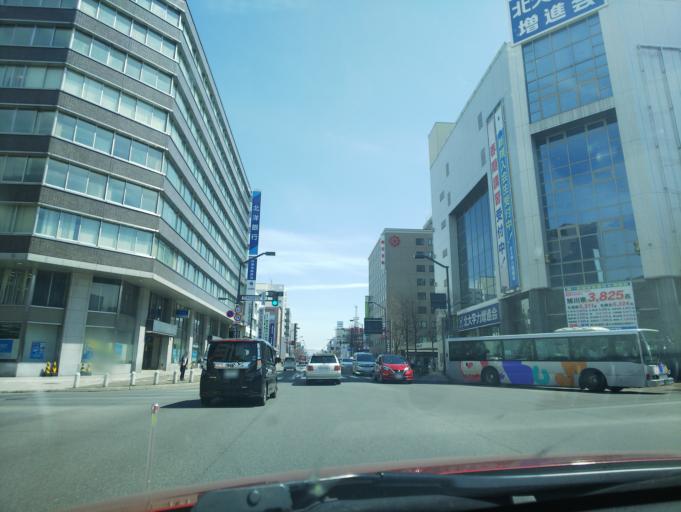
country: JP
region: Hokkaido
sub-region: Asahikawa-shi
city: Asahikawa
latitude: 43.7685
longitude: 142.3624
